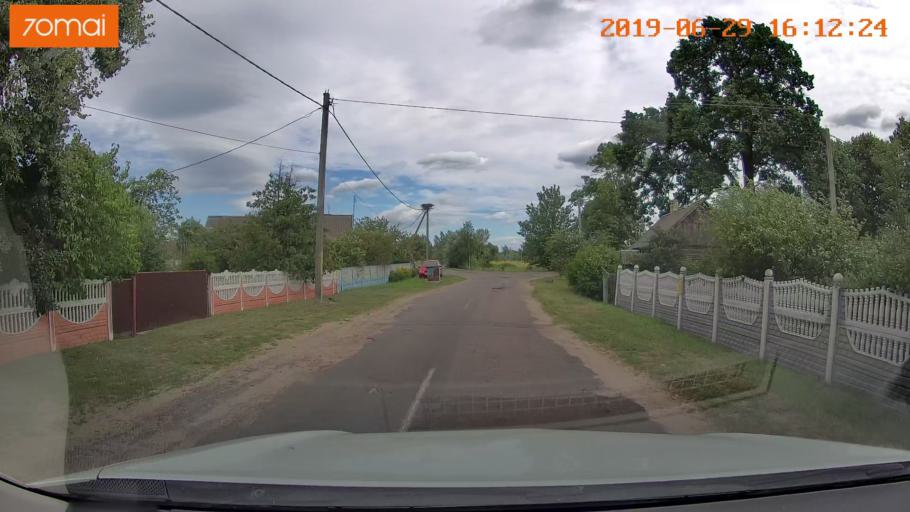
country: BY
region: Brest
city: Luninyets
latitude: 52.2007
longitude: 27.0146
